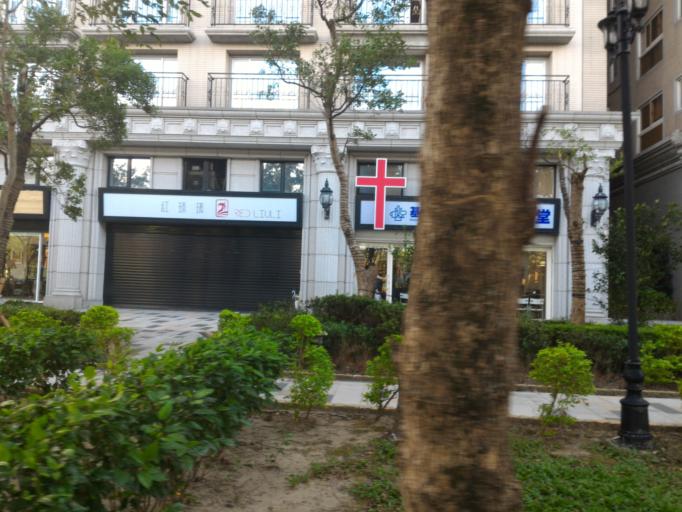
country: TW
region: Taiwan
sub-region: Taoyuan
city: Taoyuan
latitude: 24.9489
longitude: 121.3744
